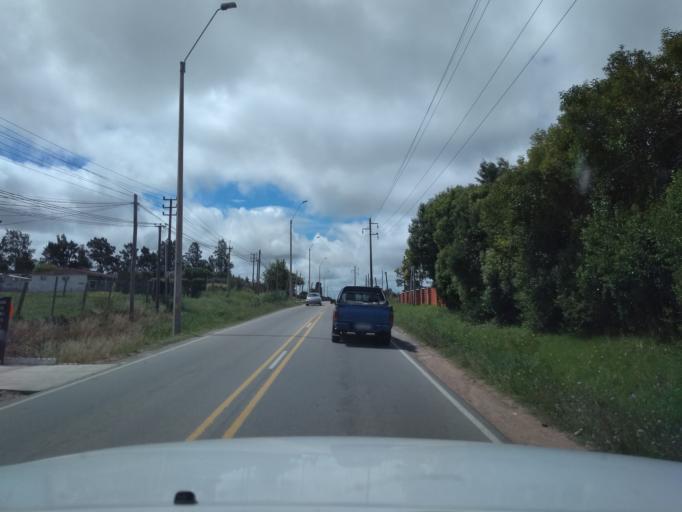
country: UY
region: Canelones
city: Pando
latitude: -34.7056
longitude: -55.9655
